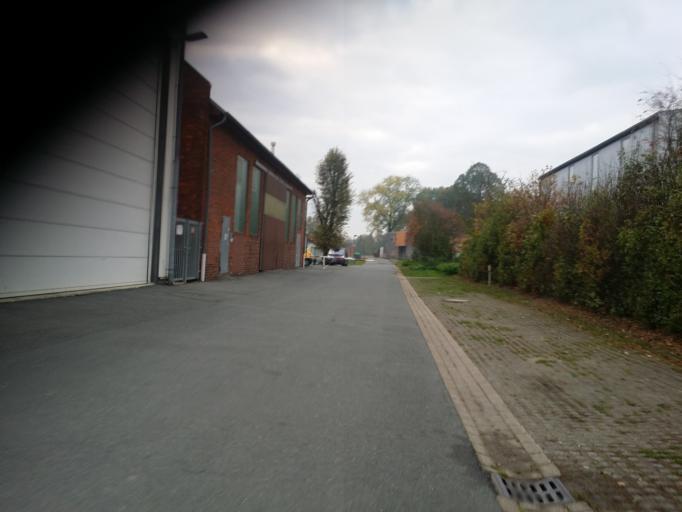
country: DE
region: Lower Saxony
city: Ritterhude
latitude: 53.1605
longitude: 8.7096
